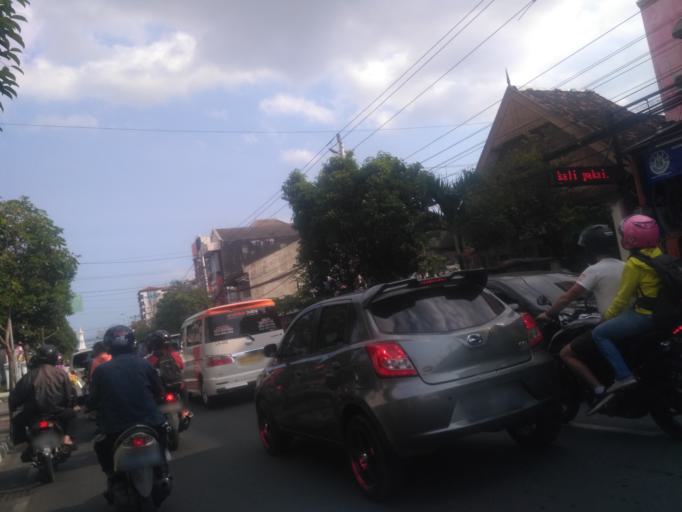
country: ID
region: Daerah Istimewa Yogyakarta
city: Yogyakarta
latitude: -7.7815
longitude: 110.3673
